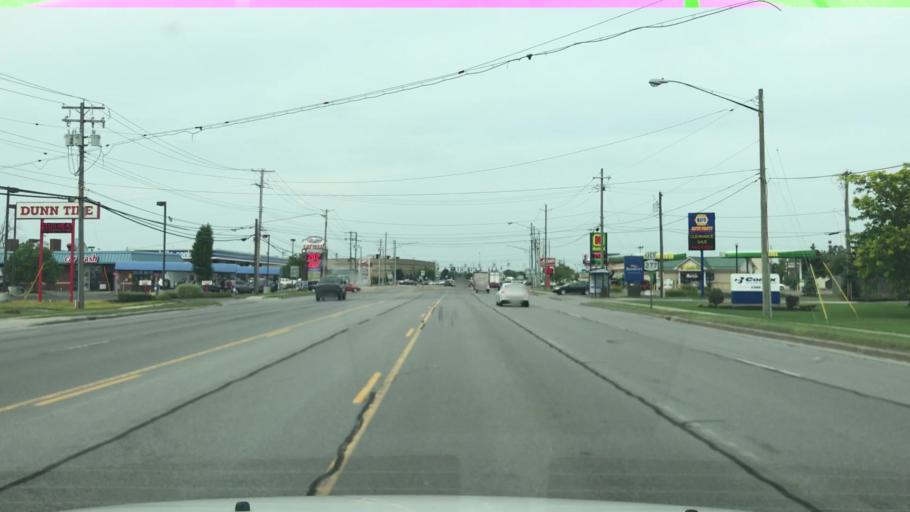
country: US
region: New York
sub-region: Erie County
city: Cheektowaga
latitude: 42.9075
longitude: -78.7507
